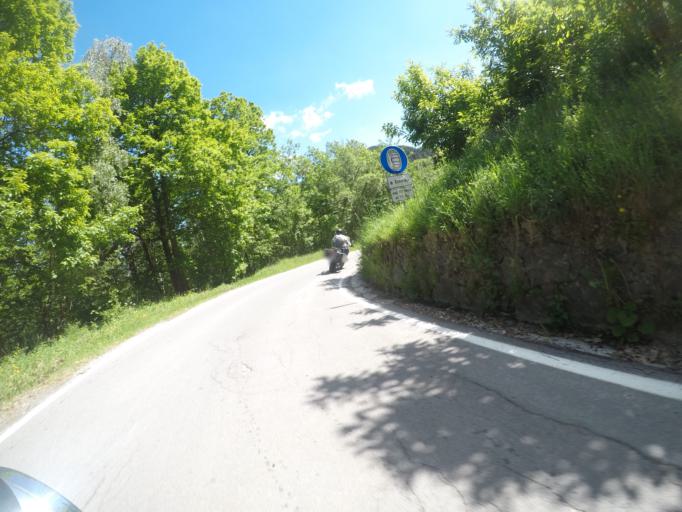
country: IT
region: Tuscany
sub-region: Provincia di Lucca
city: Careggine
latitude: 44.1027
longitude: 10.3324
